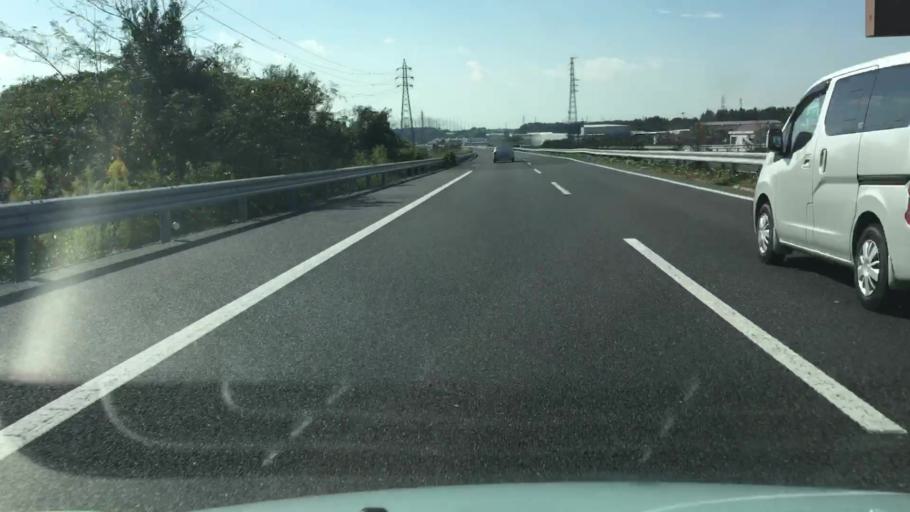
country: JP
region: Tochigi
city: Mooka
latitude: 36.4414
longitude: 139.9697
